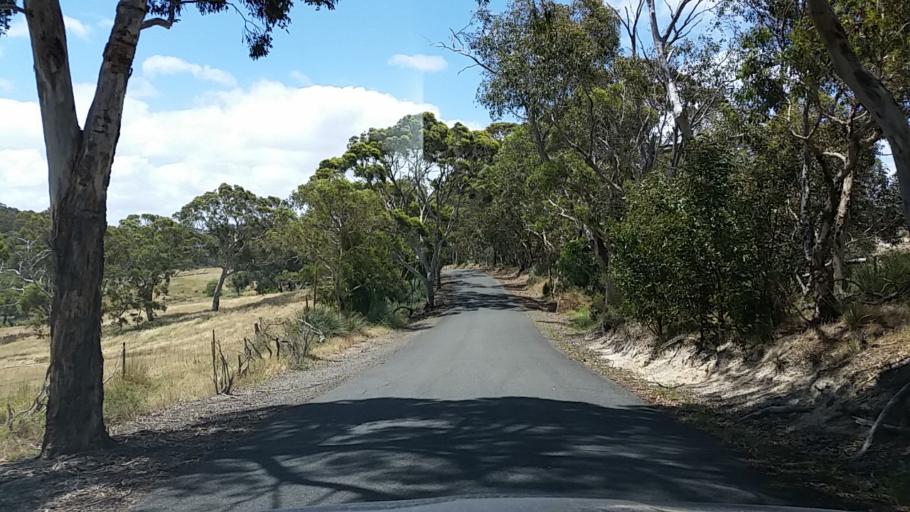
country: AU
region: South Australia
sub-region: Alexandrina
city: Mount Compass
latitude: -35.4462
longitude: 138.5922
